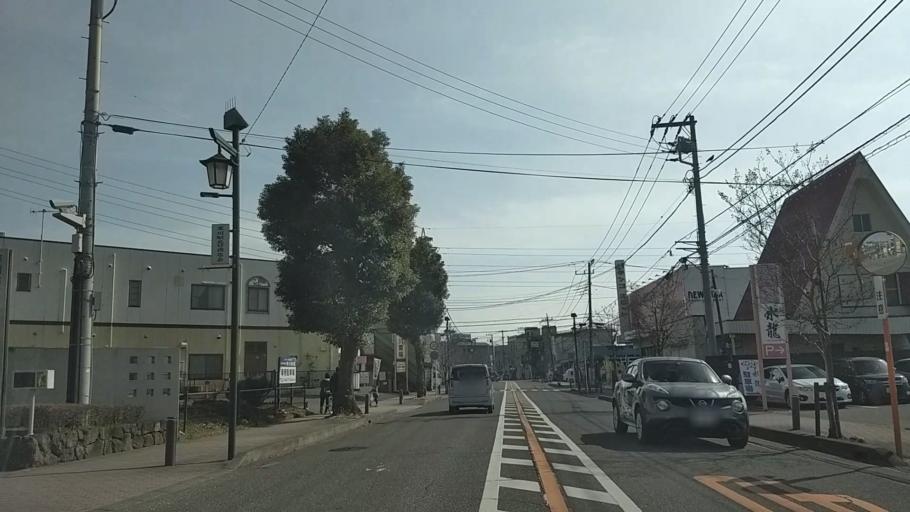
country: JP
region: Kanagawa
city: Chigasaki
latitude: 35.3711
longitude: 139.3840
